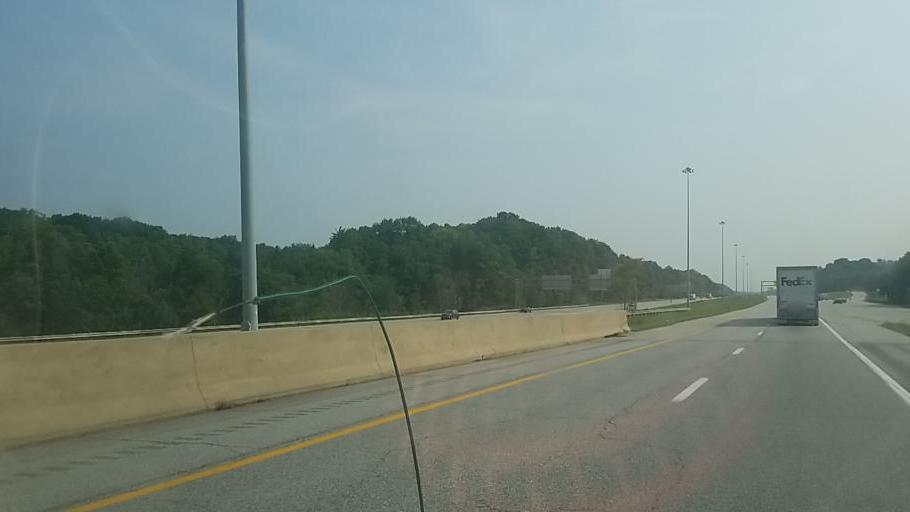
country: US
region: Ohio
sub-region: Lake County
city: Willoughby Hills
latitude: 41.6070
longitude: -81.4307
